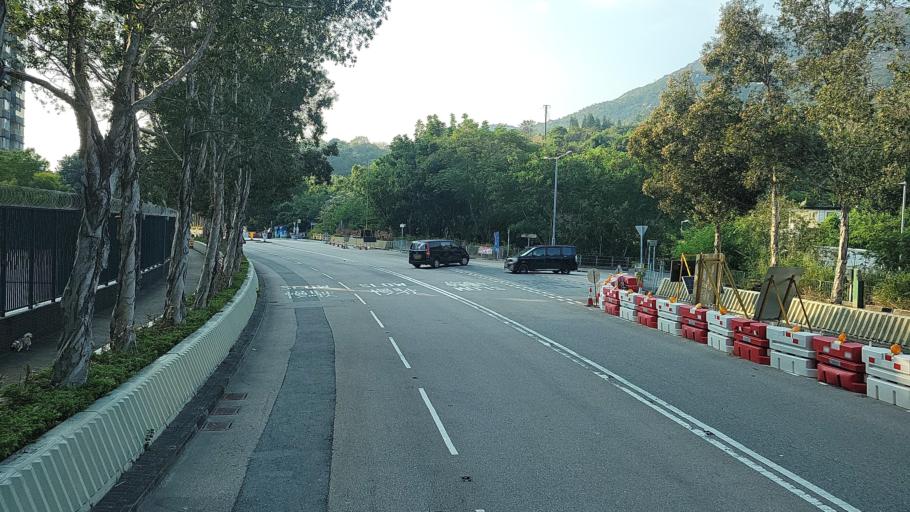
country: HK
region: Tuen Mun
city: Tuen Mun
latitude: 22.3756
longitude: 114.0008
